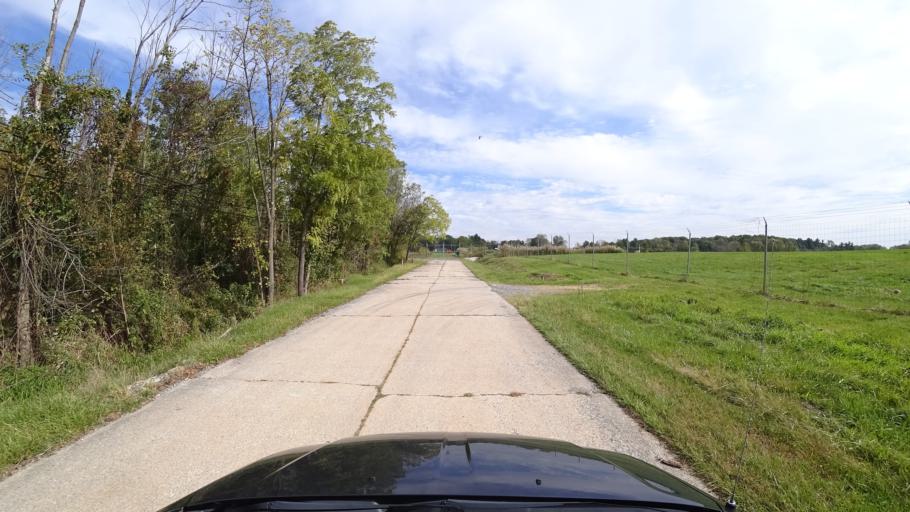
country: US
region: Indiana
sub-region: LaPorte County
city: Trail Creek
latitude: 41.7090
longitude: -86.8208
